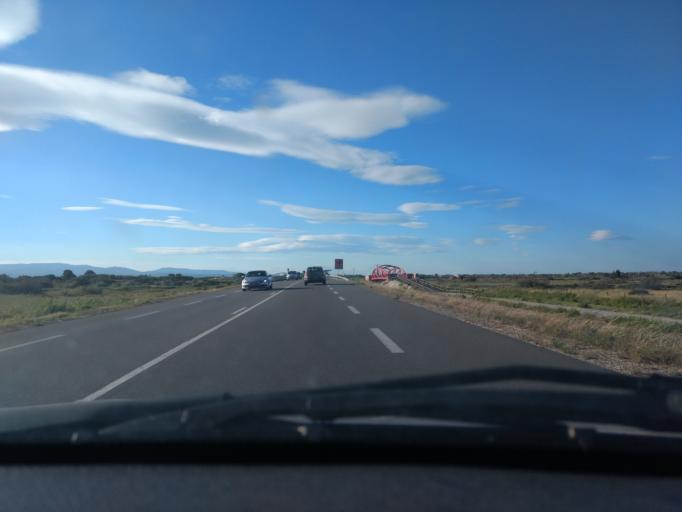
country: FR
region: Languedoc-Roussillon
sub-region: Departement des Pyrenees-Orientales
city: Torreilles
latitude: 42.7509
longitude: 3.0218
